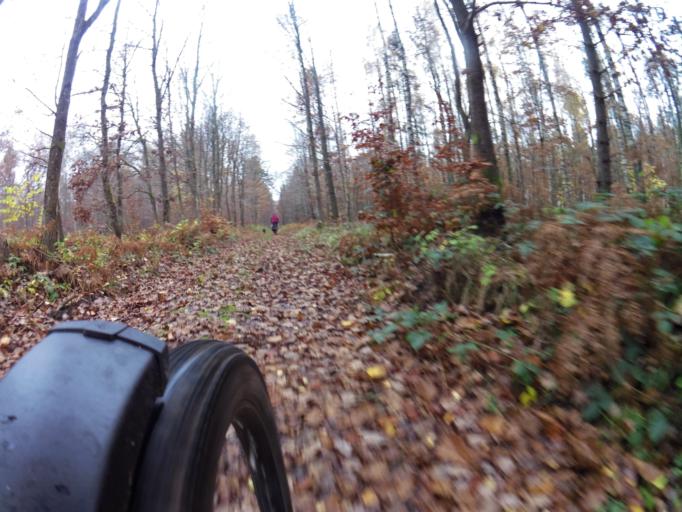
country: PL
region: Pomeranian Voivodeship
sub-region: Powiat pucki
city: Krokowa
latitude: 54.7345
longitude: 18.1309
